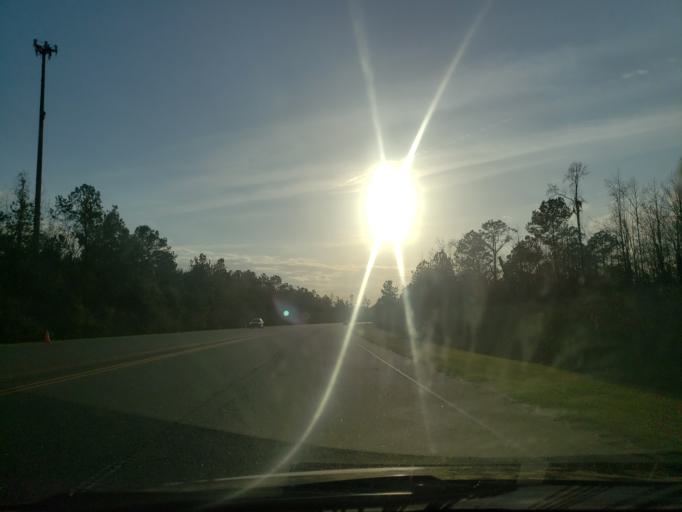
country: US
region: Georgia
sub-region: Chatham County
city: Bloomingdale
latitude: 32.1511
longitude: -81.2817
